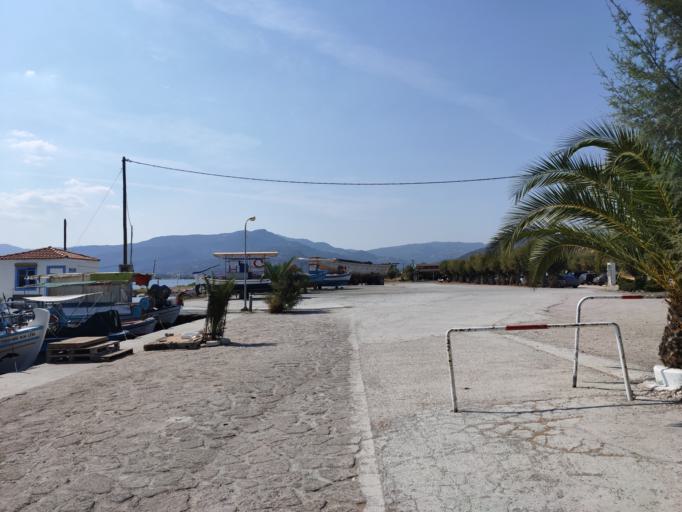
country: GR
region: North Aegean
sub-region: Nomos Lesvou
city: Kalloni
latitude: 39.2058
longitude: 26.2096
